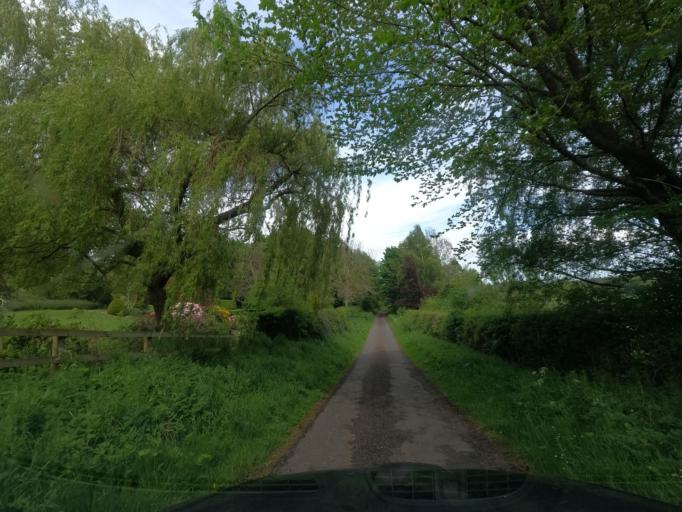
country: GB
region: England
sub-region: Northumberland
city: Kirknewton
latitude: 55.5670
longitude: -2.1016
